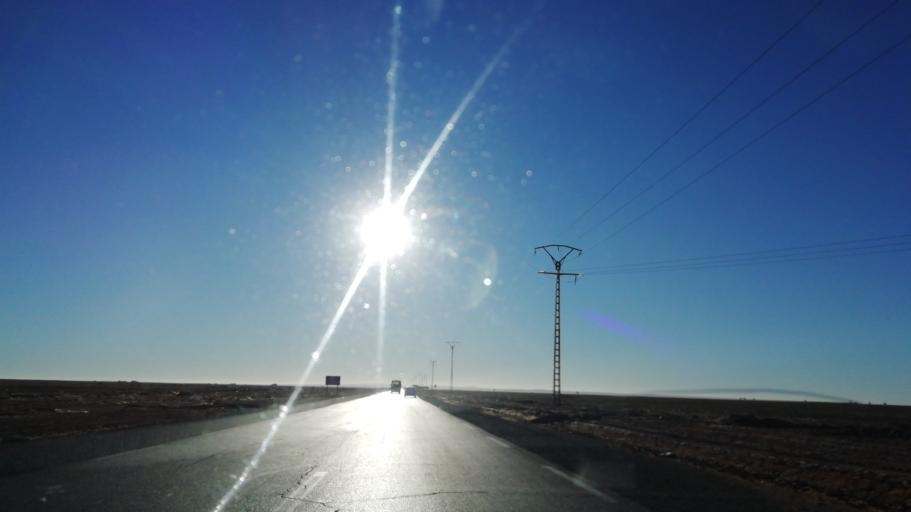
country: DZ
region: Saida
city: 'Ain el Hadjar
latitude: 34.0189
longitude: 0.1067
